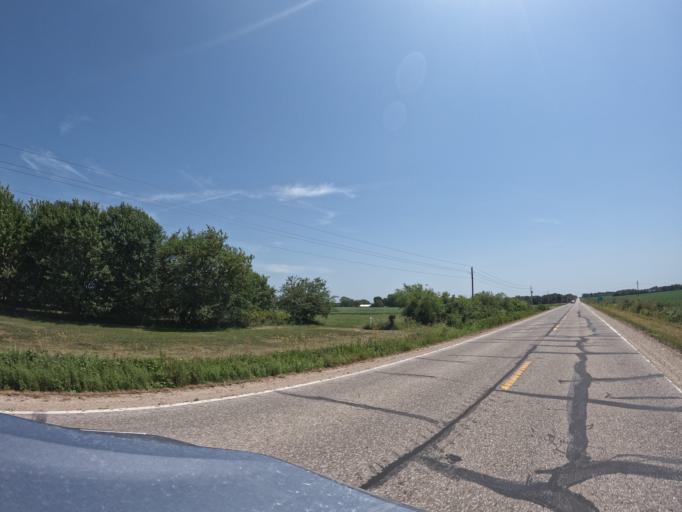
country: US
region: Iowa
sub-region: Henry County
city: Mount Pleasant
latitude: 40.9718
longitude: -91.6124
